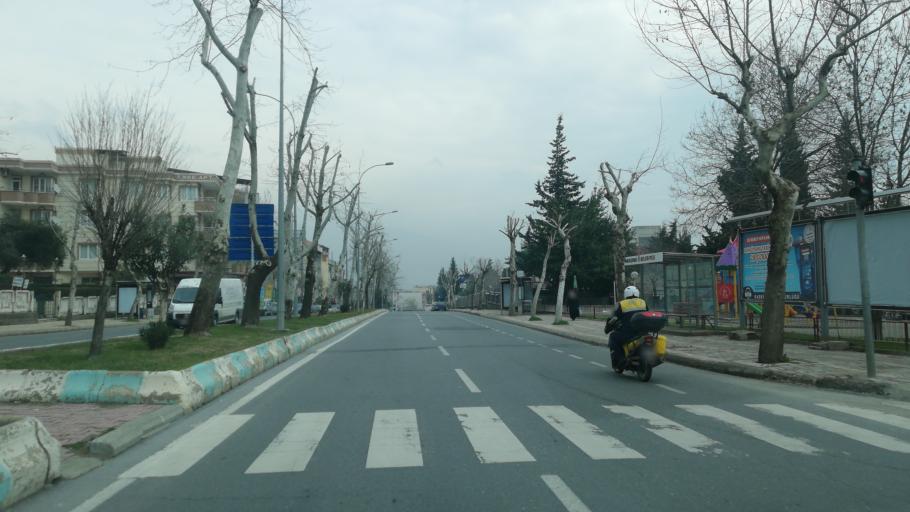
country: TR
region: Kahramanmaras
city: Kahramanmaras
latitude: 37.5882
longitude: 36.9094
